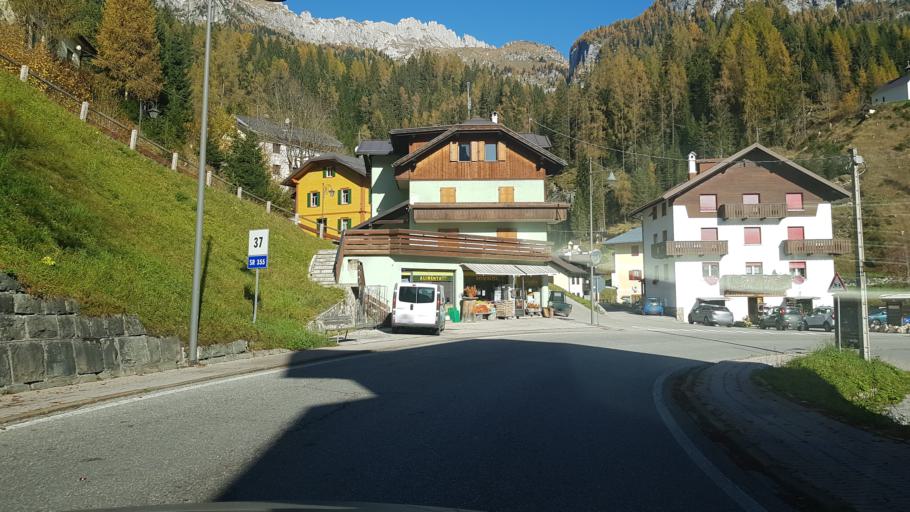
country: IT
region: Veneto
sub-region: Provincia di Belluno
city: Granvilla
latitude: 46.5667
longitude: 12.6875
